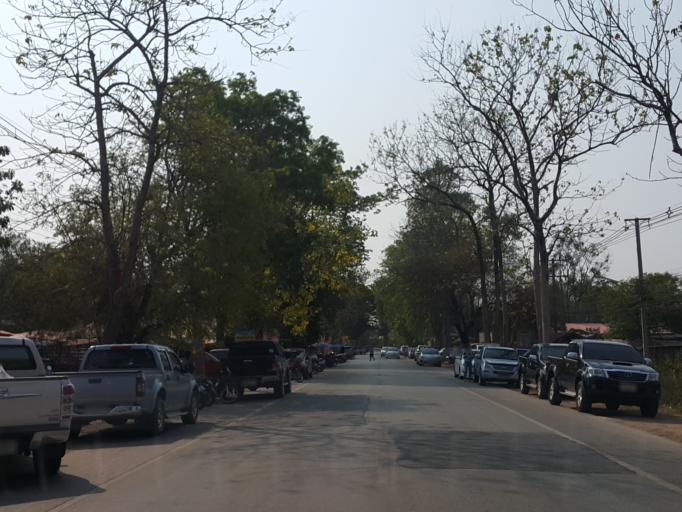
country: TH
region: Sukhothai
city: Ban Na
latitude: 17.0232
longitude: 99.6858
